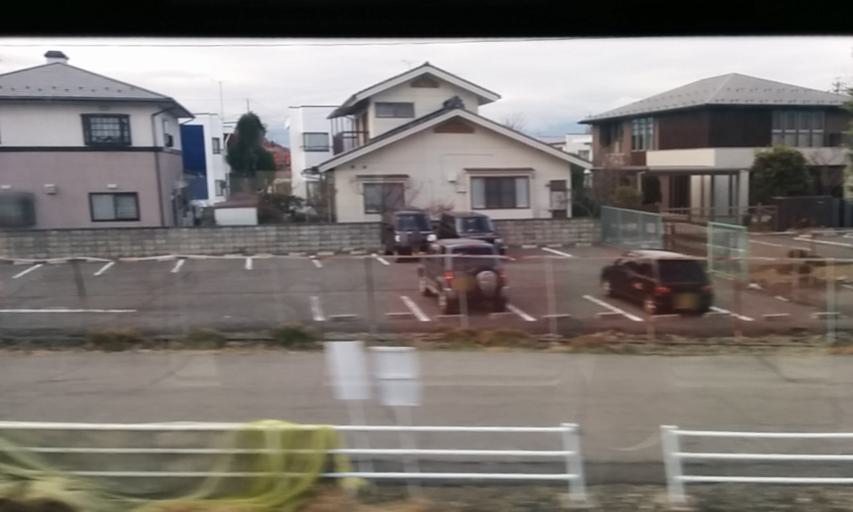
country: JP
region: Nagano
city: Matsumoto
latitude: 36.1865
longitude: 137.9606
